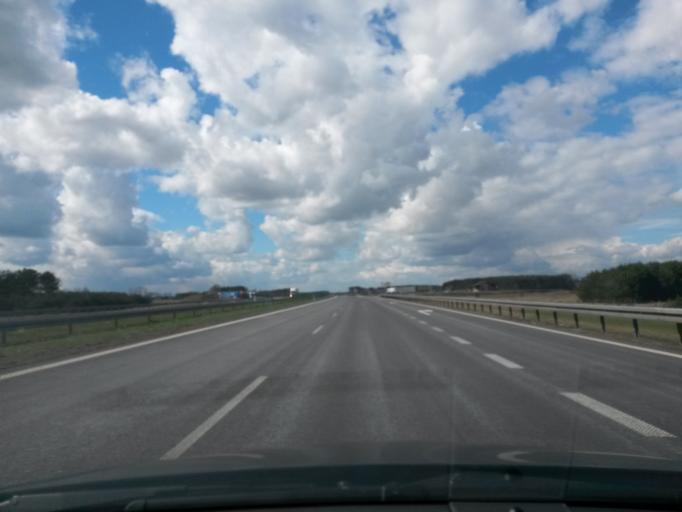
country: PL
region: Greater Poland Voivodeship
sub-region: Powiat kolski
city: Dabie
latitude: 52.0955
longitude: 18.7768
